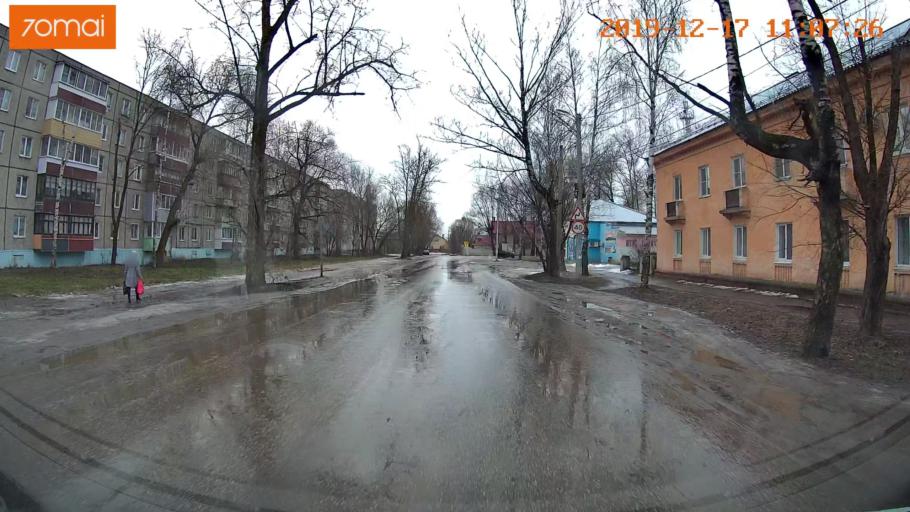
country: RU
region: Vladimir
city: Gus'-Khrustal'nyy
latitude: 55.6107
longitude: 40.6446
